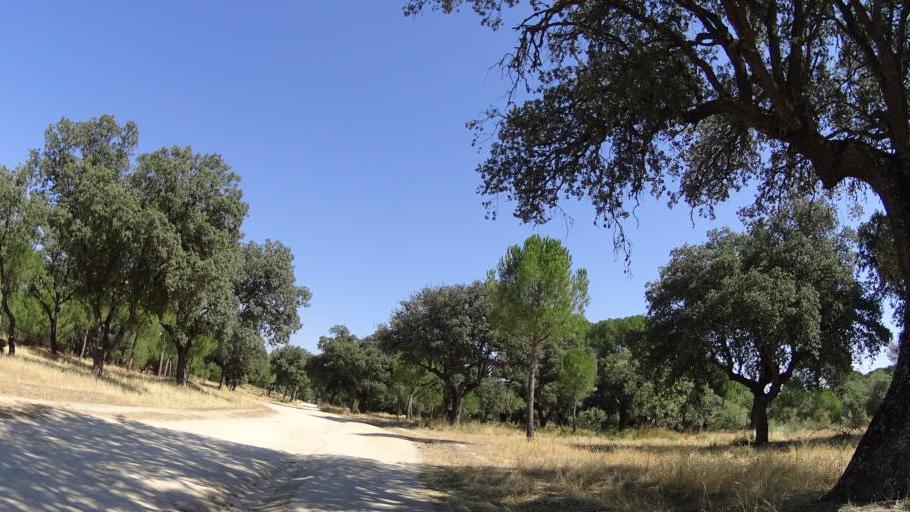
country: ES
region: Madrid
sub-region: Provincia de Madrid
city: Boadilla del Monte
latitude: 40.4232
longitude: -3.8544
